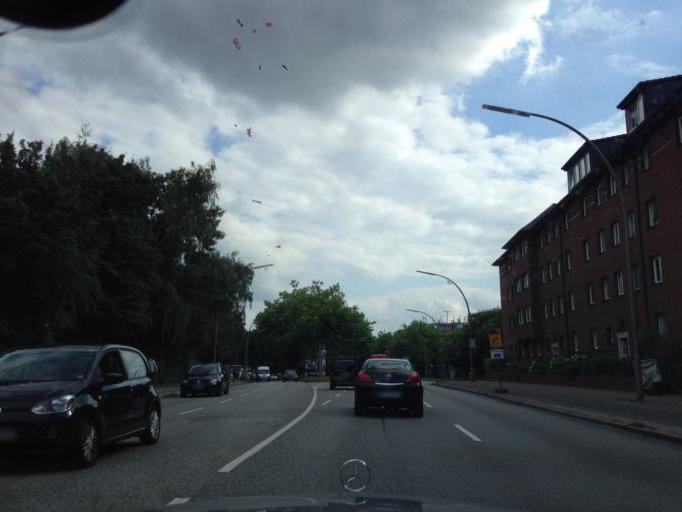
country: DE
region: Hamburg
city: Marienthal
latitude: 53.5567
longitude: 10.0825
